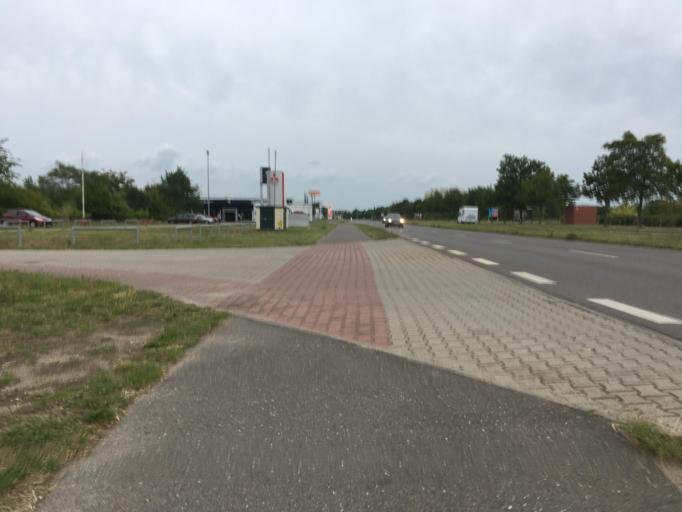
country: DE
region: Brandenburg
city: Meyenburg
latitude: 53.0725
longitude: 14.2517
